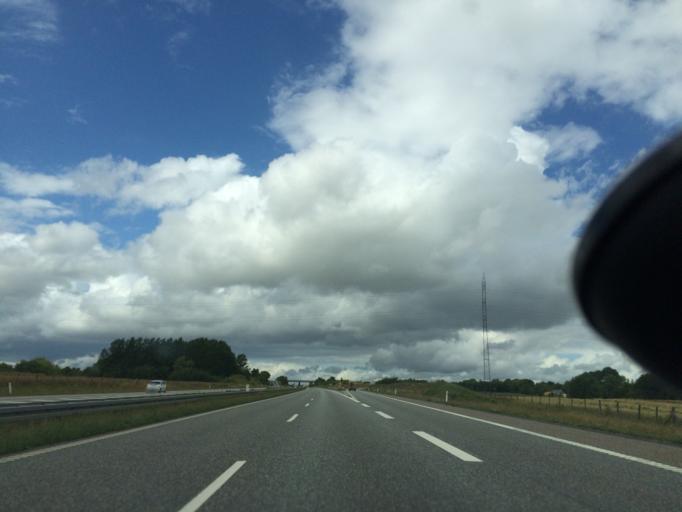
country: DK
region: Central Jutland
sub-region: Arhus Kommune
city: Framlev
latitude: 56.1533
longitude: 10.0177
